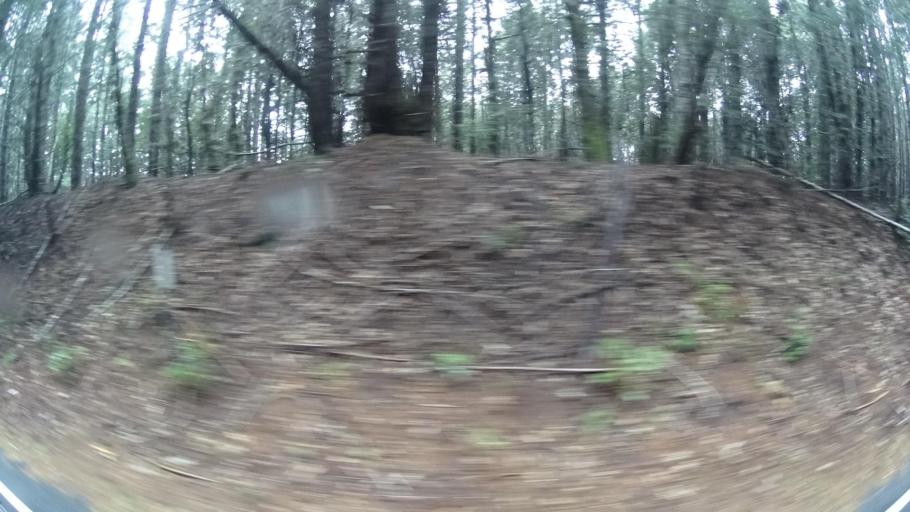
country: US
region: California
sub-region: Humboldt County
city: Westhaven-Moonstone
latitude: 41.2139
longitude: -123.9572
